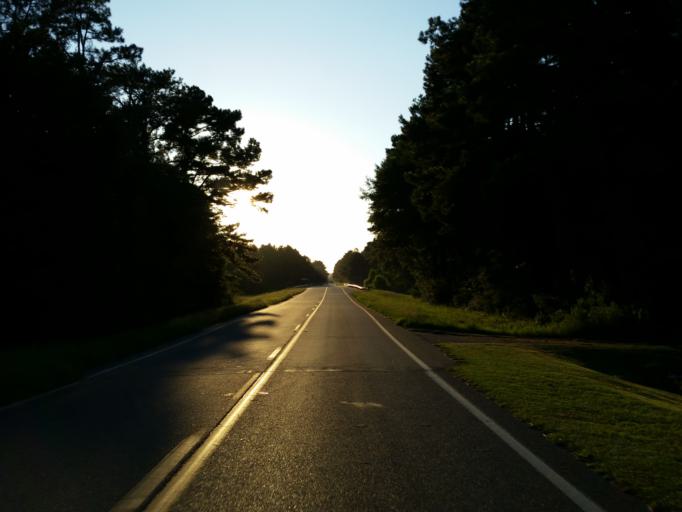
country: US
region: Georgia
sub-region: Berrien County
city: Ray City
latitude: 31.1728
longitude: -83.1129
